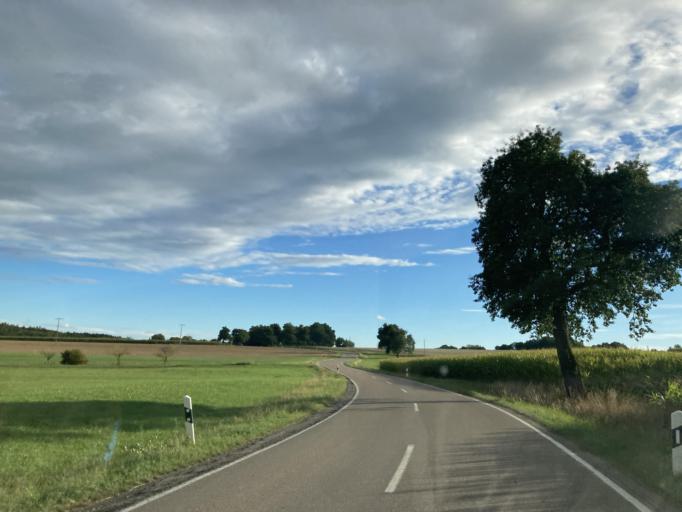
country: DE
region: Bavaria
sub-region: Swabia
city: Amerdingen
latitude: 48.7075
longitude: 10.4366
